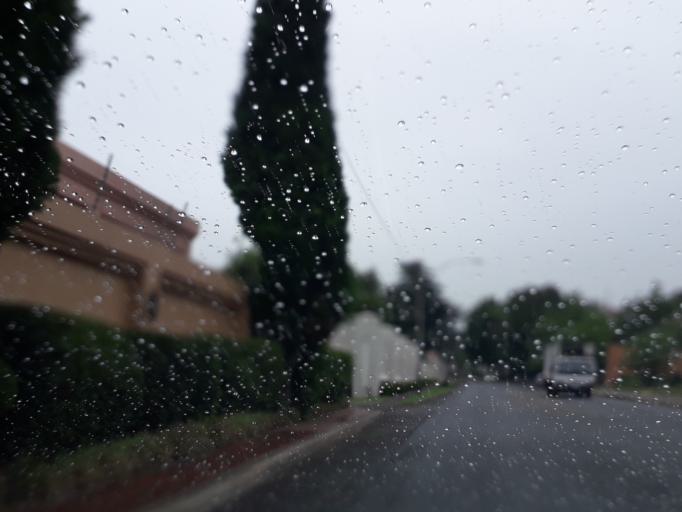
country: ZA
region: Gauteng
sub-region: City of Johannesburg Metropolitan Municipality
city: Johannesburg
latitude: -26.1291
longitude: 28.0459
